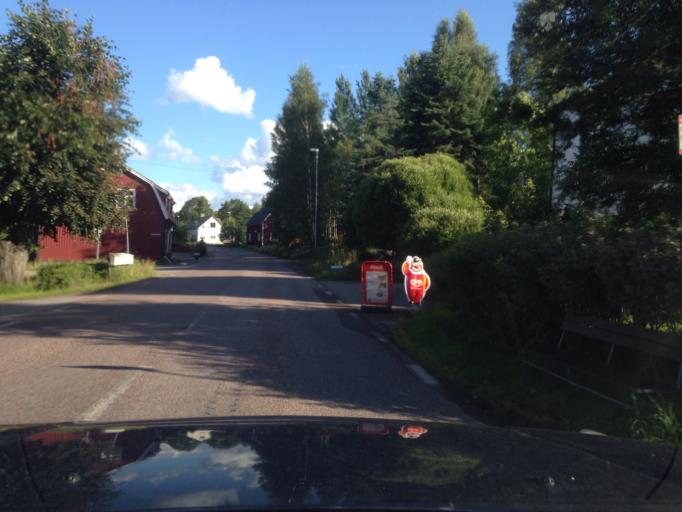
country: SE
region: Dalarna
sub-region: Ludvika Kommun
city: Grangesberg
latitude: 60.1463
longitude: 14.9863
